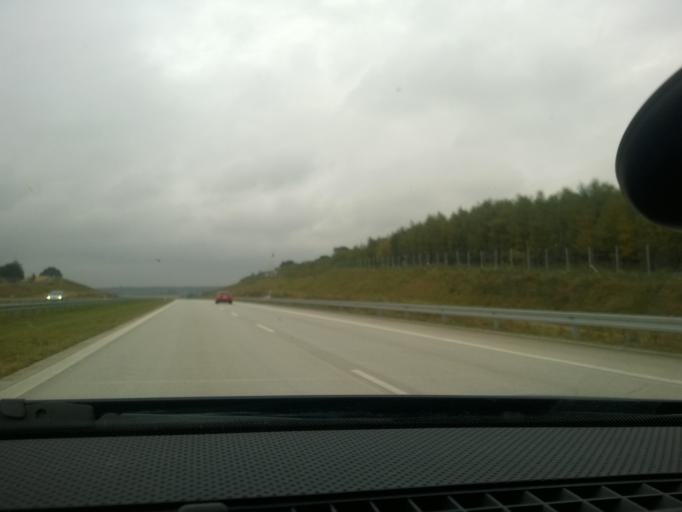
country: PL
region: Lodz Voivodeship
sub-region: Powiat zgierski
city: Strykow
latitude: 51.8288
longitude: 19.6533
